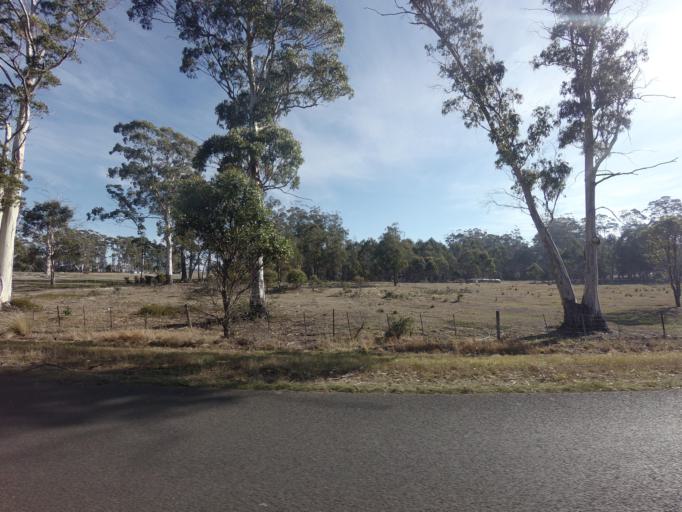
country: AU
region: Tasmania
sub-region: Sorell
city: Sorell
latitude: -42.4653
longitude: 147.4613
